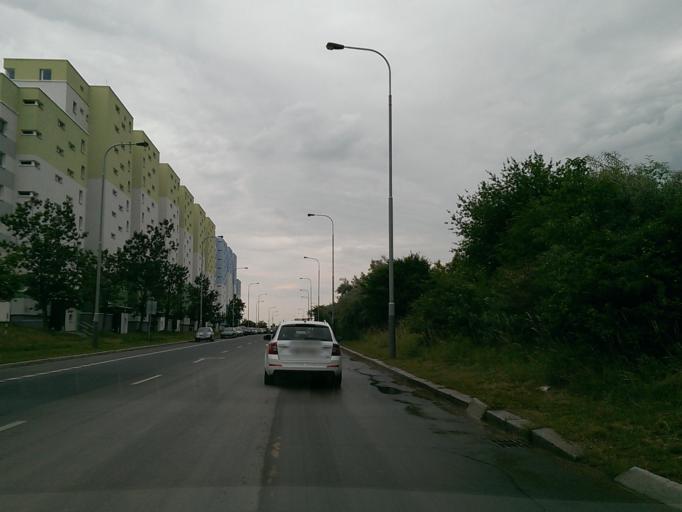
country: CZ
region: Central Bohemia
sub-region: Okres Praha-Zapad
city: Pruhonice
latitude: 50.0419
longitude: 14.5670
